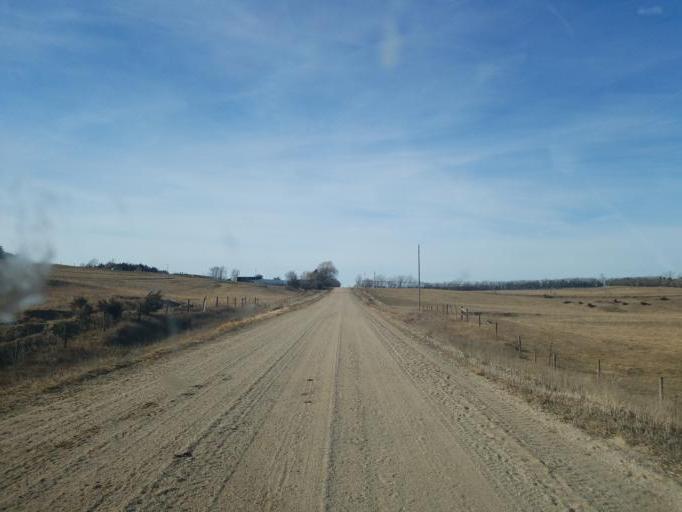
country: US
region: Nebraska
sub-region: Knox County
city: Center
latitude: 42.6262
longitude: -97.8089
